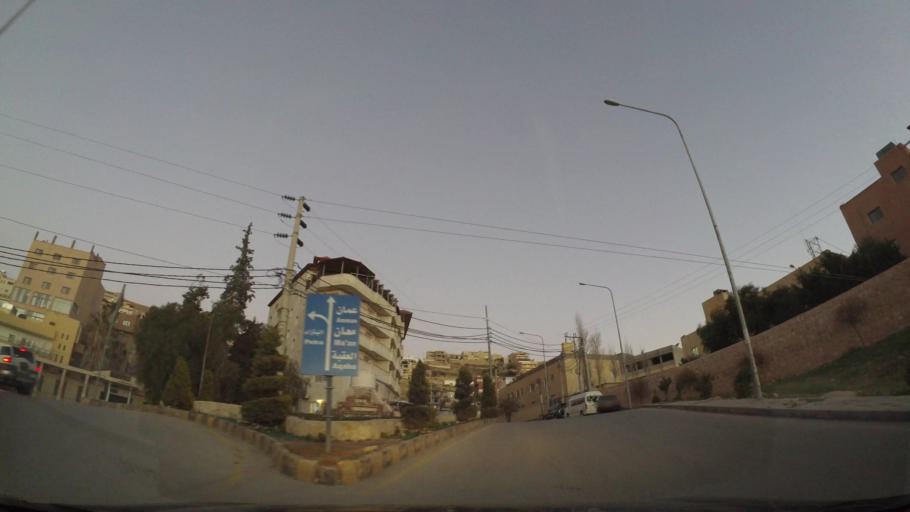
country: JO
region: Ma'an
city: Petra
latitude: 30.3185
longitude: 35.4813
